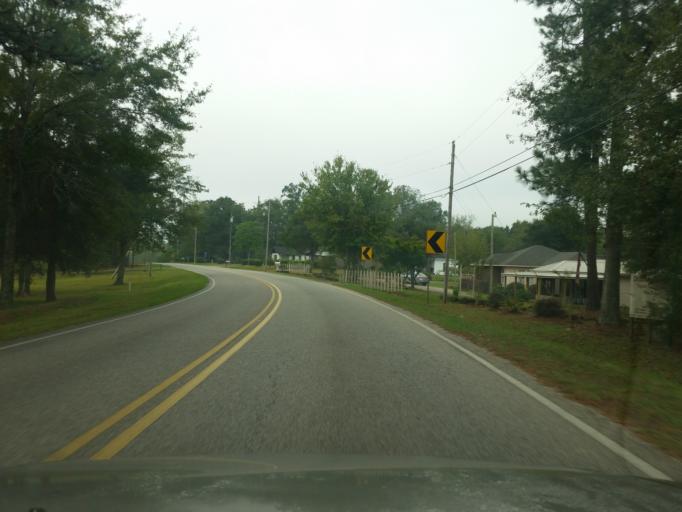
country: US
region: Alabama
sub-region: Baldwin County
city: Bay Minette
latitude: 30.8620
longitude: -87.7998
